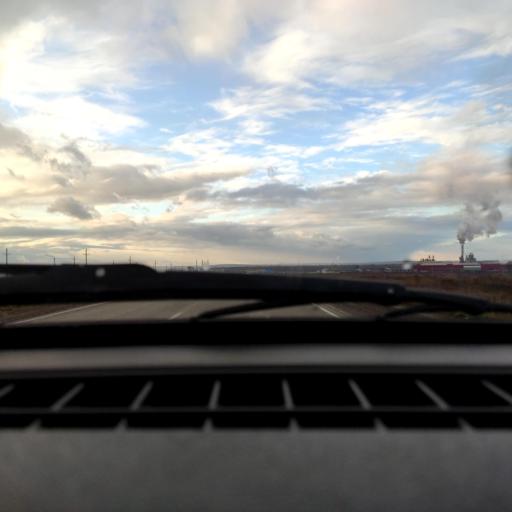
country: RU
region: Bashkortostan
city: Iglino
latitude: 54.7557
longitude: 56.2813
